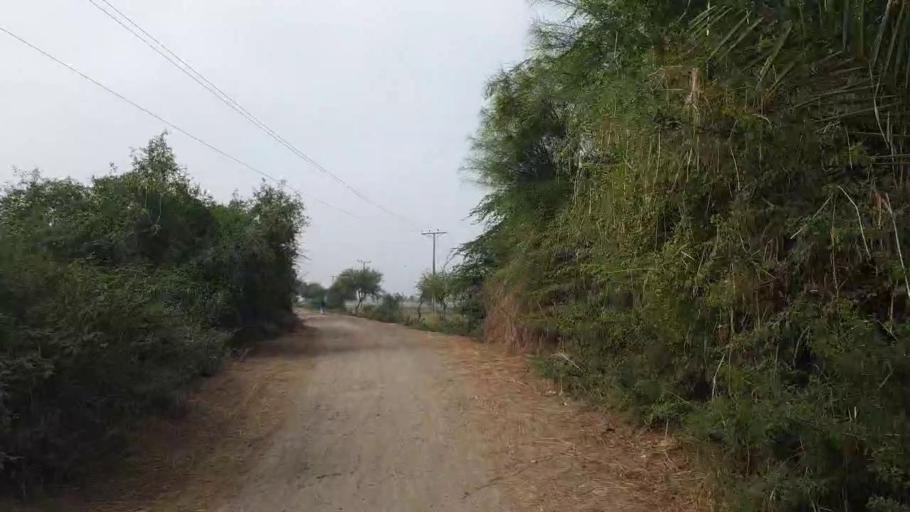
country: PK
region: Sindh
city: Matli
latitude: 24.9694
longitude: 68.5980
